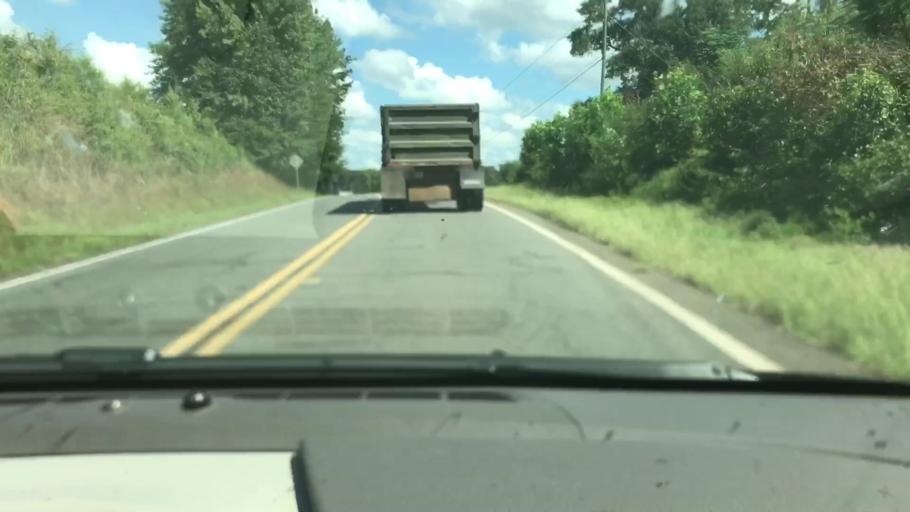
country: US
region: Alabama
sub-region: Chambers County
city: Valley
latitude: 32.8303
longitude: -85.0348
